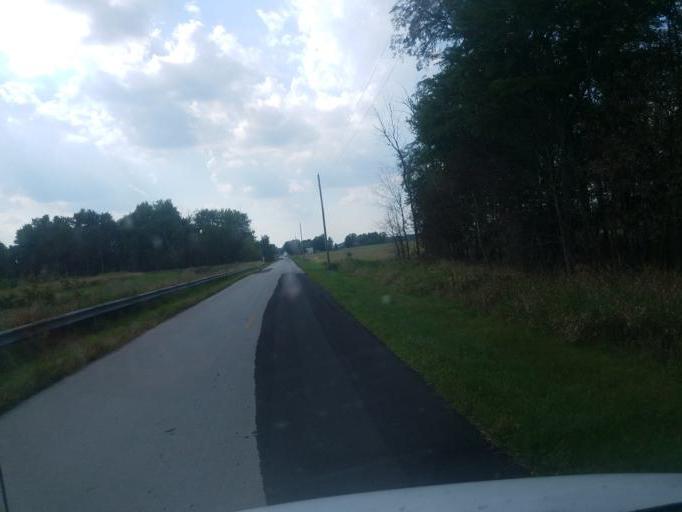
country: US
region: Ohio
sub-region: Hardin County
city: Kenton
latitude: 40.7458
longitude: -83.6042
